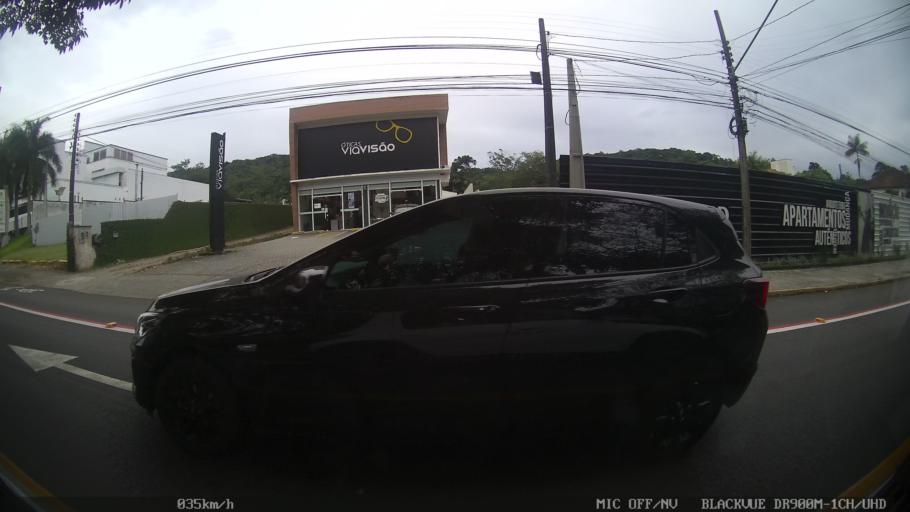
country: BR
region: Santa Catarina
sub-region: Joinville
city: Joinville
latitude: -26.3054
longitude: -48.8628
